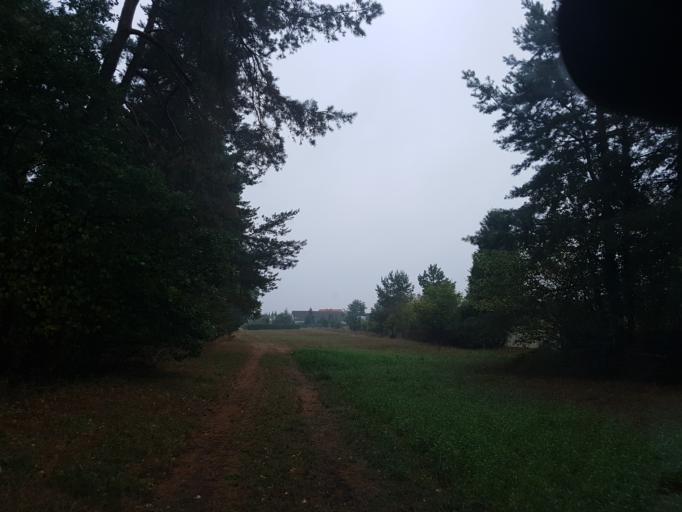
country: DE
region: Brandenburg
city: Wiesenburg
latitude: 52.0842
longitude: 12.4482
